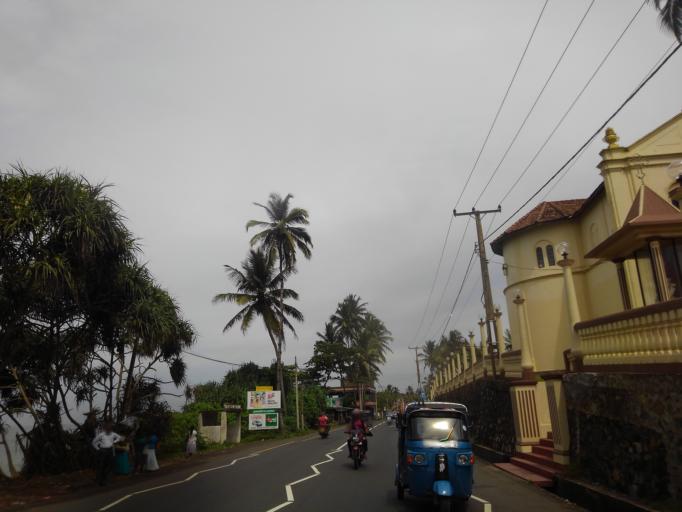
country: LK
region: Western
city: Beruwala
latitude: 6.4815
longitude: 79.9833
